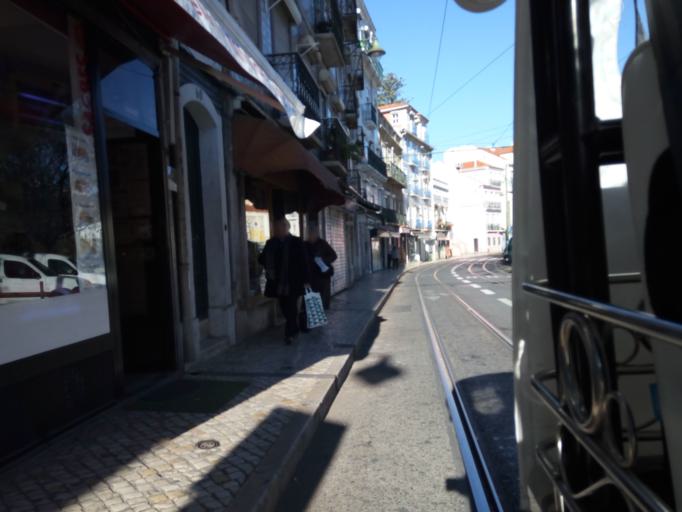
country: PT
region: Lisbon
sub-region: Lisbon
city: Lisbon
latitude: 38.7202
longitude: -9.1298
